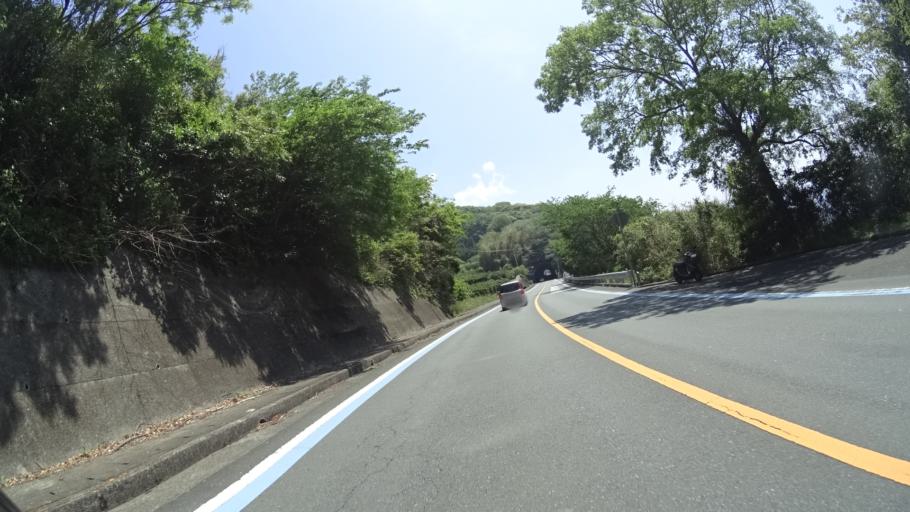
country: JP
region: Ehime
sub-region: Nishiuwa-gun
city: Ikata-cho
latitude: 33.4907
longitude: 132.3442
